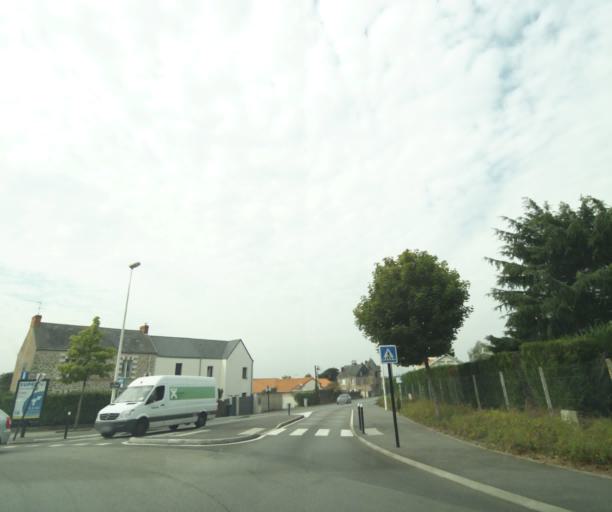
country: FR
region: Pays de la Loire
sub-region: Departement de la Loire-Atlantique
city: Saint-Herblain
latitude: 47.2101
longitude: -1.6288
